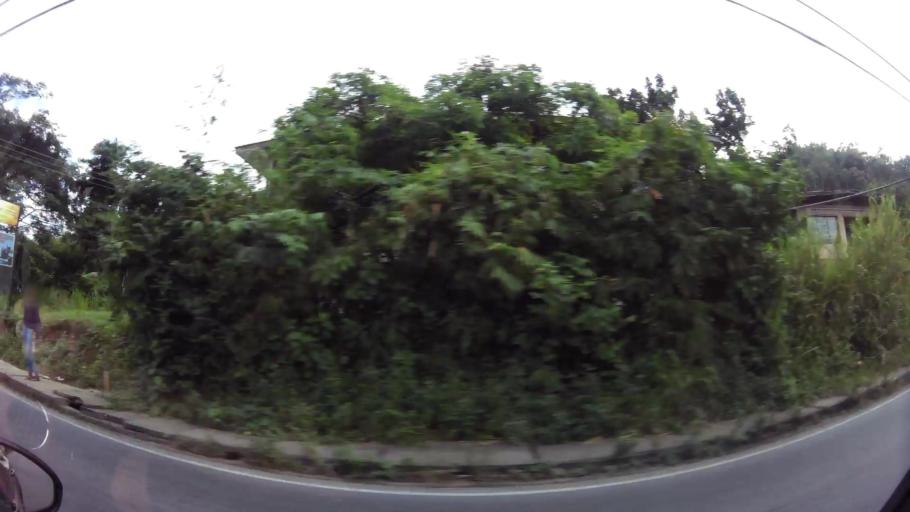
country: TT
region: San Juan/Laventille
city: Laventille
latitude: 10.6654
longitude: -61.4491
